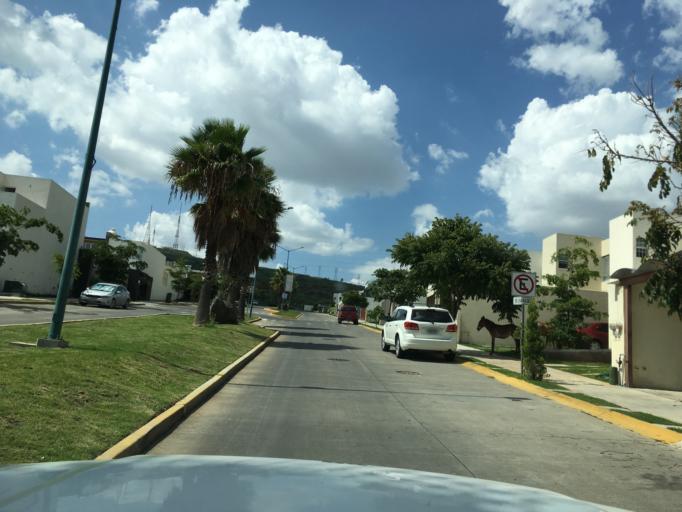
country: MX
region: Jalisco
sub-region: Tlajomulco de Zuniga
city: Altus Bosques
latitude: 20.5843
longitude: -103.3653
